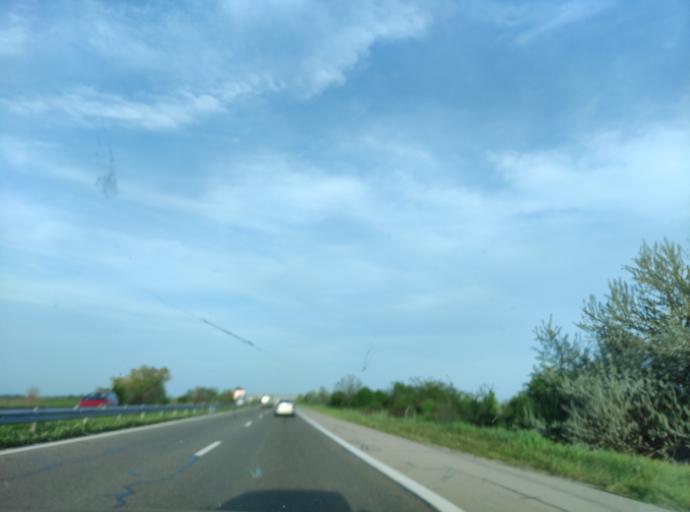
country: BG
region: Plovdiv
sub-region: Obshtina Suedinenie
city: Suedinenie
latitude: 42.2028
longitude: 24.5817
